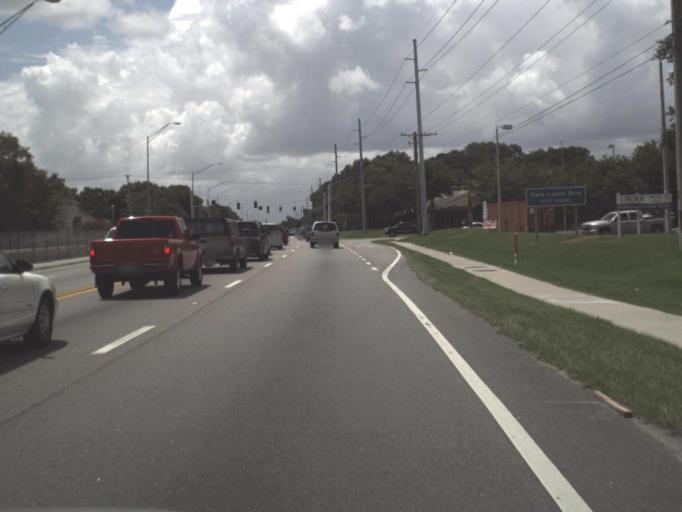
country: US
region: Florida
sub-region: Hillsborough County
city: Carrollwood
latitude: 28.0359
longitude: -82.4903
